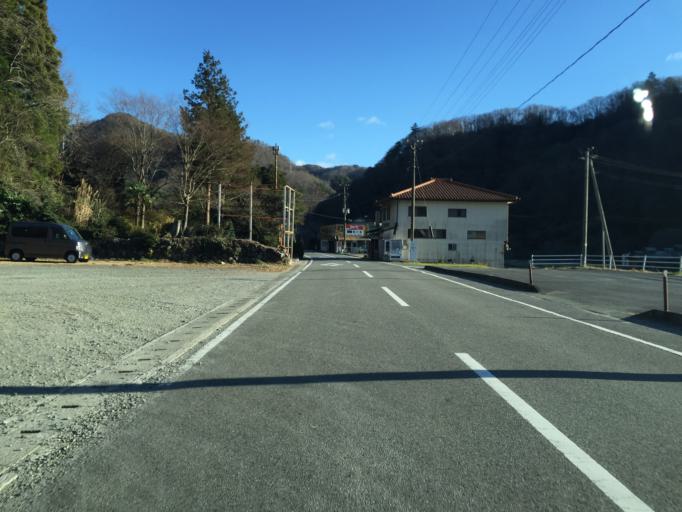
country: JP
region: Fukushima
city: Iwaki
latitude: 37.1799
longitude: 140.8247
